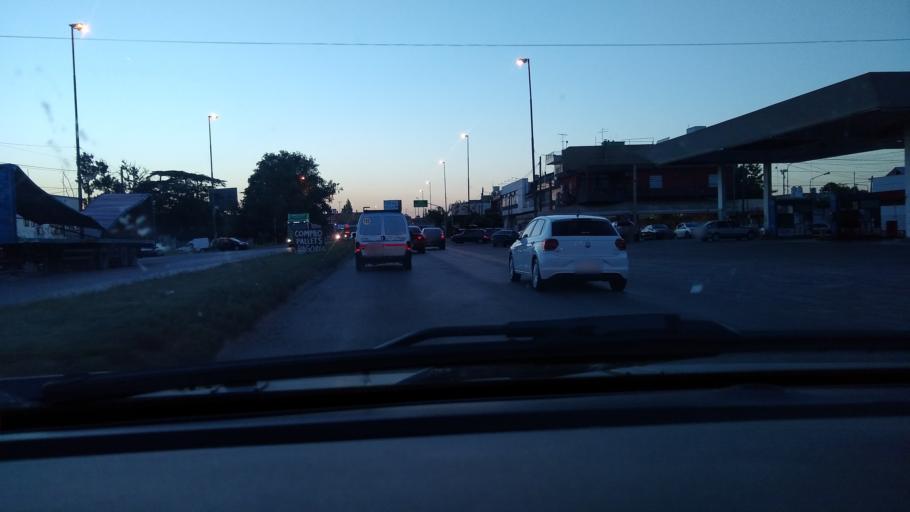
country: AR
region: Buenos Aires
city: San Justo
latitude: -34.6804
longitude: -58.5807
